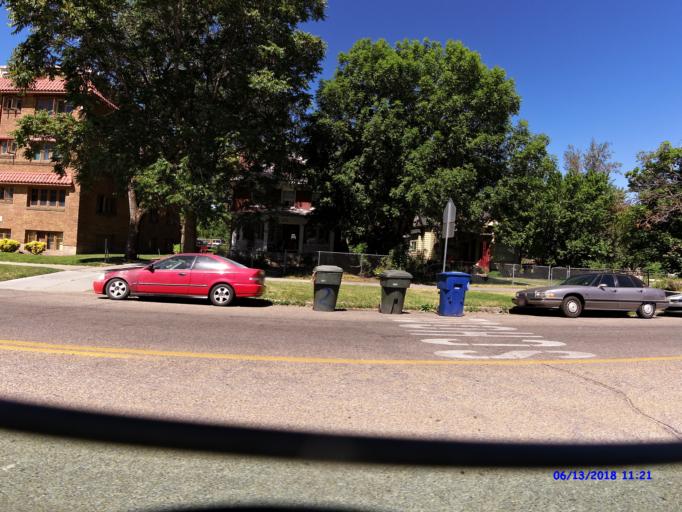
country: US
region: Utah
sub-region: Weber County
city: Ogden
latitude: 41.2212
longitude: -111.9593
